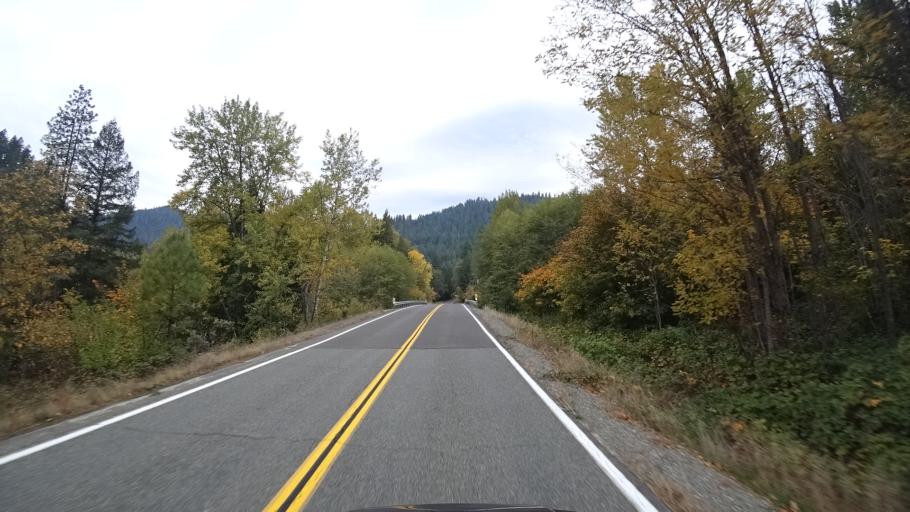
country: US
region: California
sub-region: Siskiyou County
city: Happy Camp
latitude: 41.8793
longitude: -123.4204
